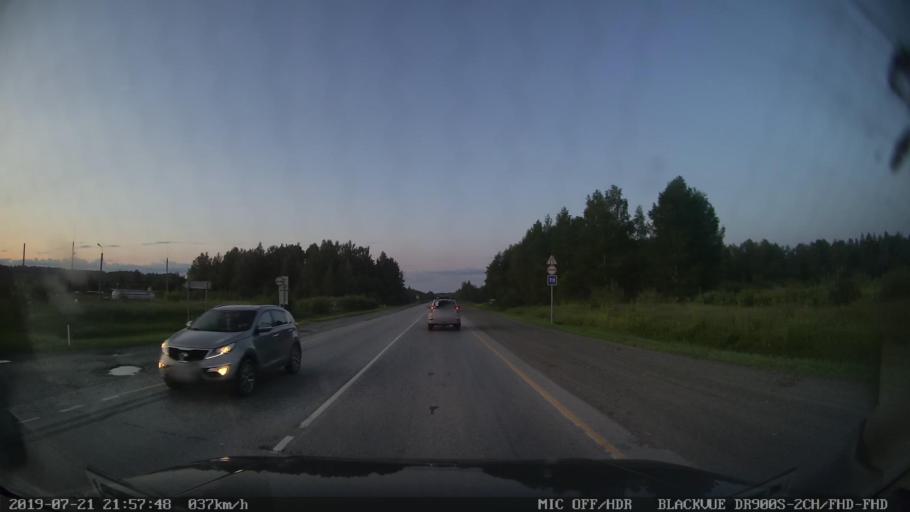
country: RU
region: Perm
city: Chaykovskaya
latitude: 58.0015
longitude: 55.4940
